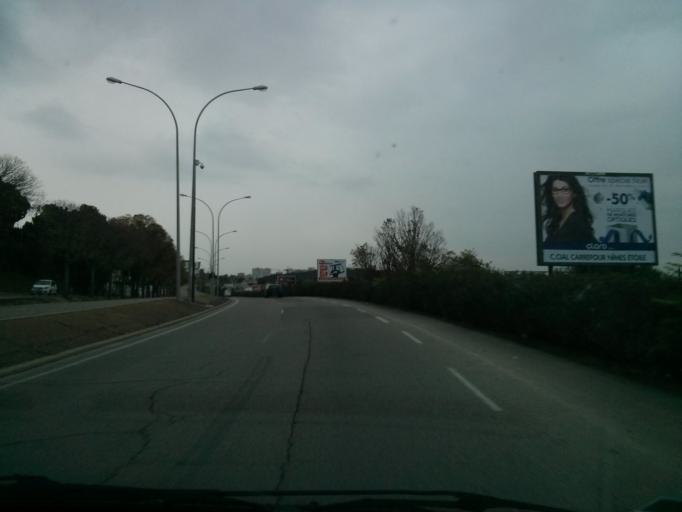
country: FR
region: Languedoc-Roussillon
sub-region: Departement du Gard
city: Milhaud
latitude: 43.8157
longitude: 4.3146
